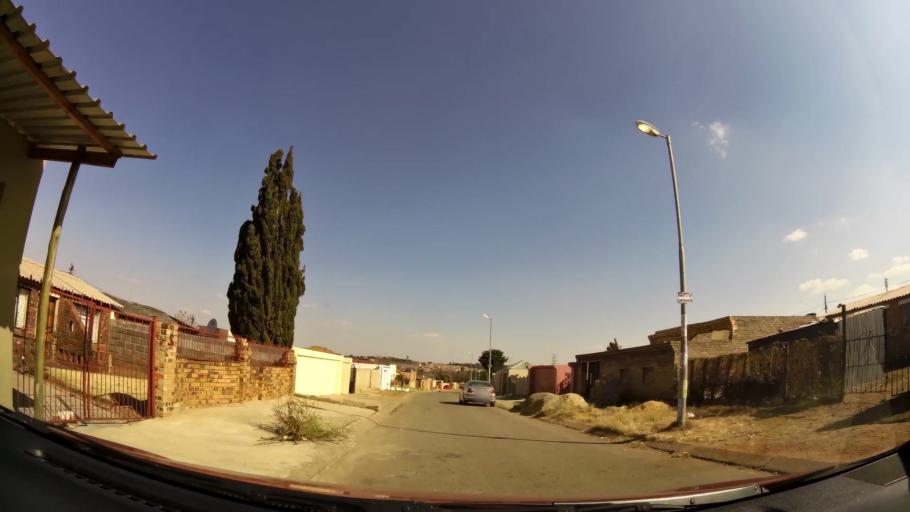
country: ZA
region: Gauteng
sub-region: City of Johannesburg Metropolitan Municipality
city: Soweto
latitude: -26.2346
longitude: 27.8801
